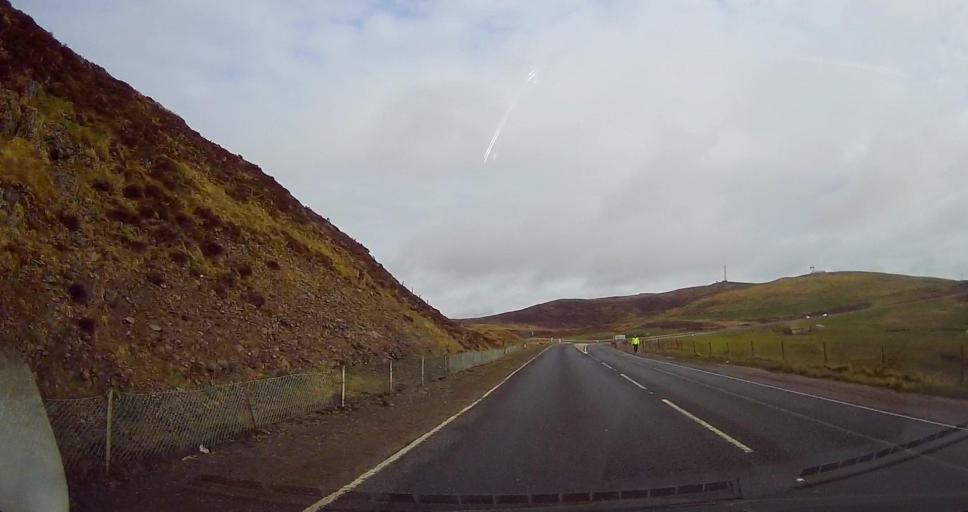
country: GB
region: Scotland
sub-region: Shetland Islands
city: Lerwick
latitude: 60.1348
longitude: -1.2140
